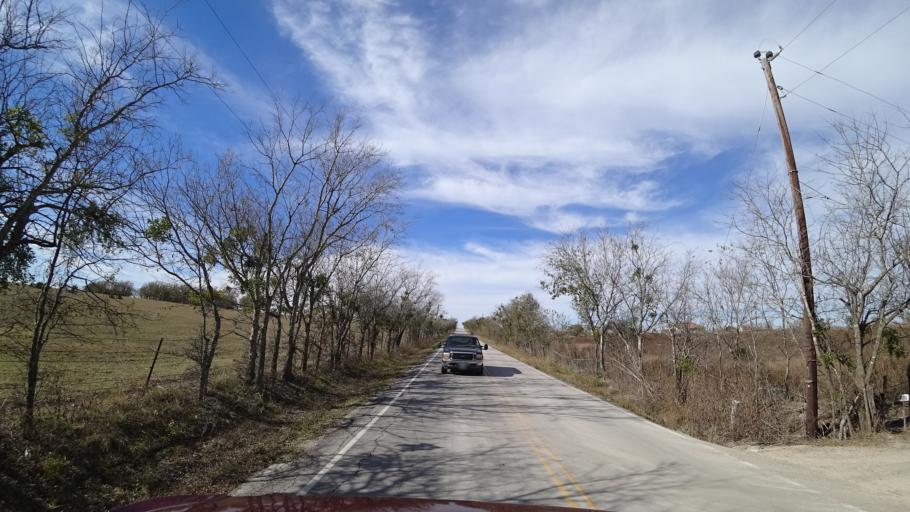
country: US
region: Texas
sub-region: Travis County
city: Onion Creek
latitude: 30.1048
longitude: -97.7352
